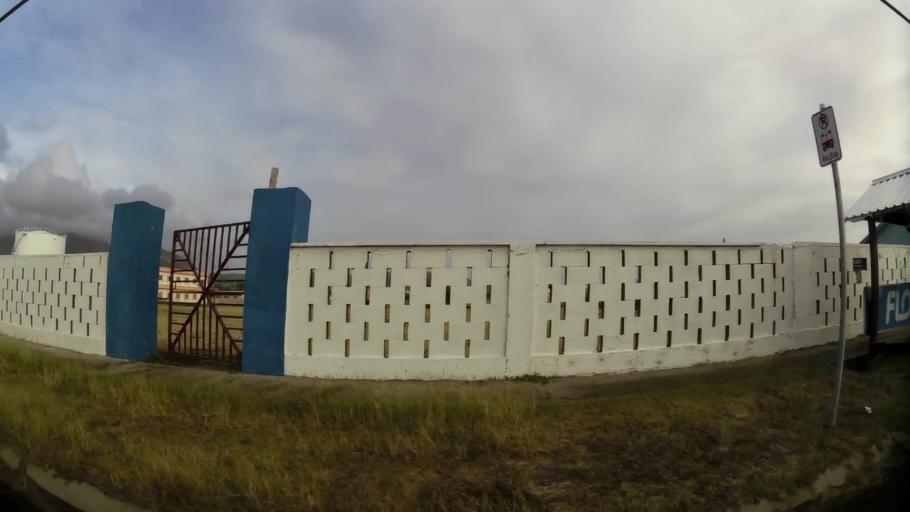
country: KN
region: Saint George Basseterre
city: Basseterre
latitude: 17.2946
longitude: -62.7158
